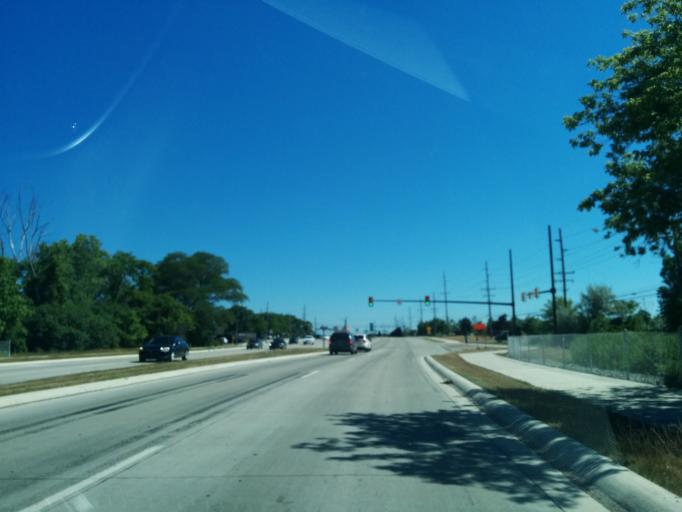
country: US
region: Michigan
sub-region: Oakland County
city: West Bloomfield Township
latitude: 42.5328
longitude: -83.3604
